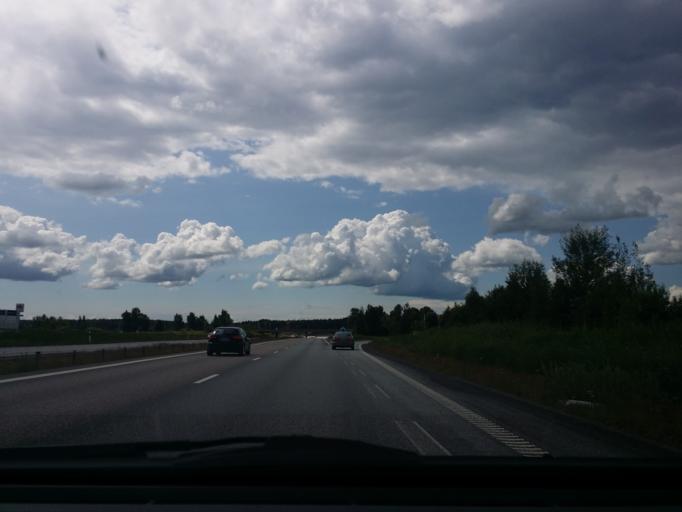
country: SE
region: Vaestmanland
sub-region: Kopings Kommun
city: Koping
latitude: 59.5242
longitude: 15.9732
